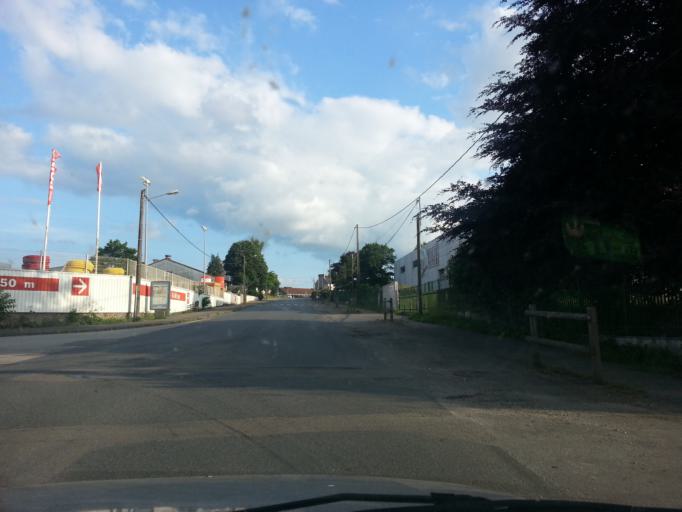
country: FR
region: Brittany
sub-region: Departement du Finistere
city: Carhaix-Plouguer
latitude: 48.2820
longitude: -3.5619
